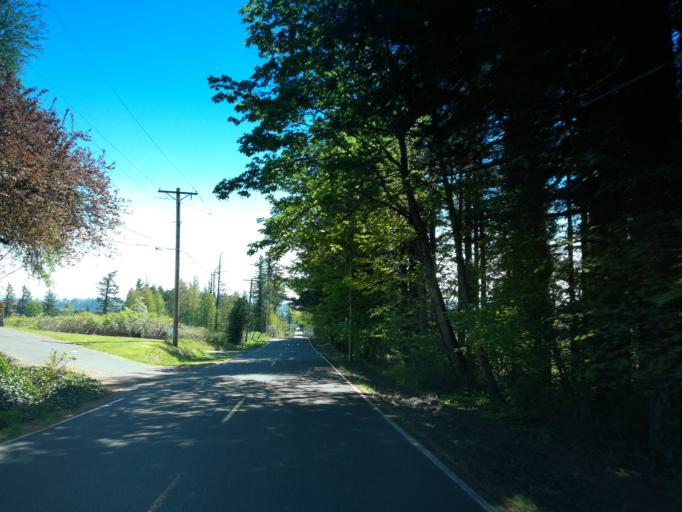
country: US
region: Oregon
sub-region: Multnomah County
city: Troutdale
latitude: 45.5285
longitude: -122.3523
